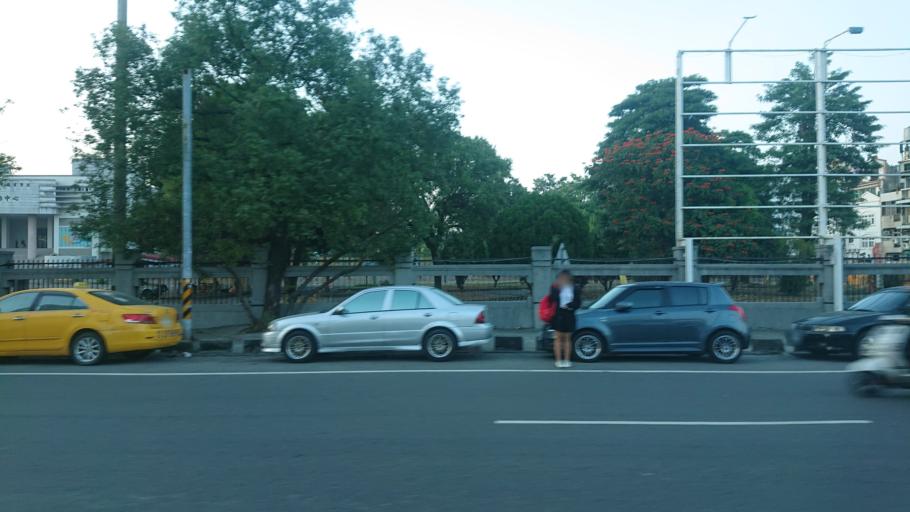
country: TW
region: Taiwan
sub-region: Tainan
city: Tainan
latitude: 23.0148
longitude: 120.2347
